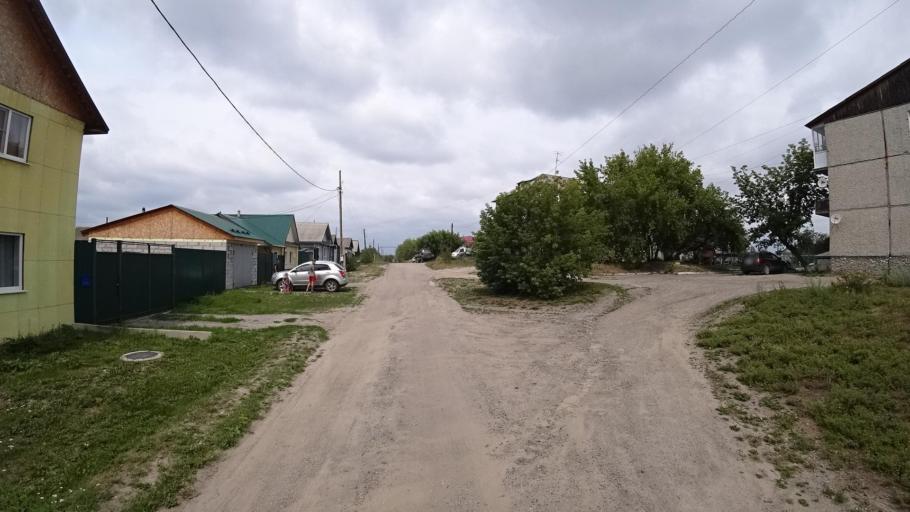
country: RU
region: Sverdlovsk
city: Kamyshlov
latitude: 56.8360
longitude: 62.7202
